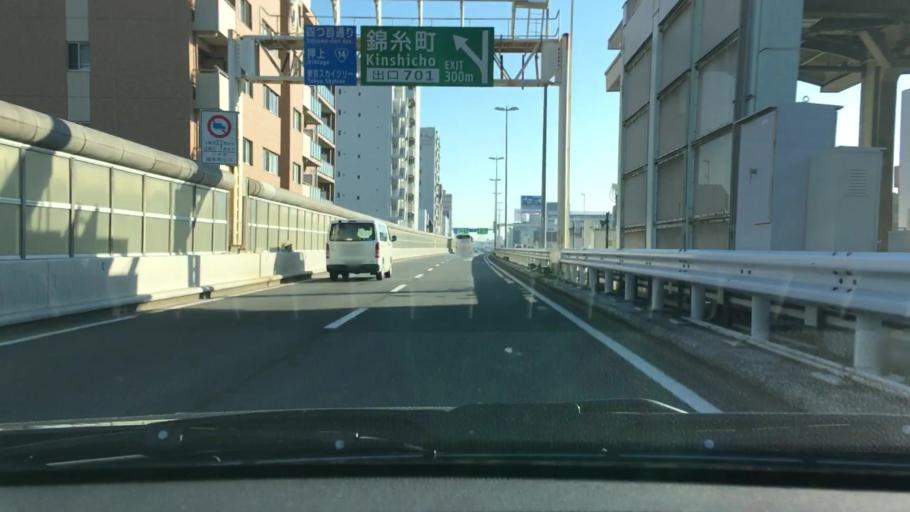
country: JP
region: Tokyo
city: Urayasu
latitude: 35.6929
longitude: 139.8095
